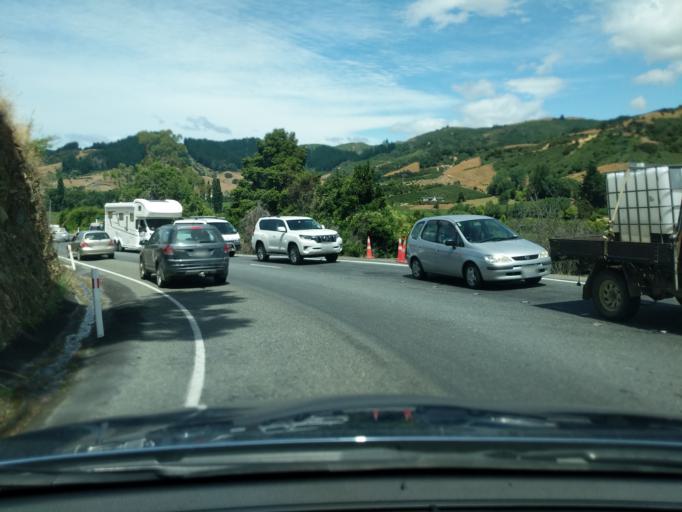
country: NZ
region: Tasman
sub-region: Tasman District
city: Motueka
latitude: -41.0534
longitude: 172.9631
